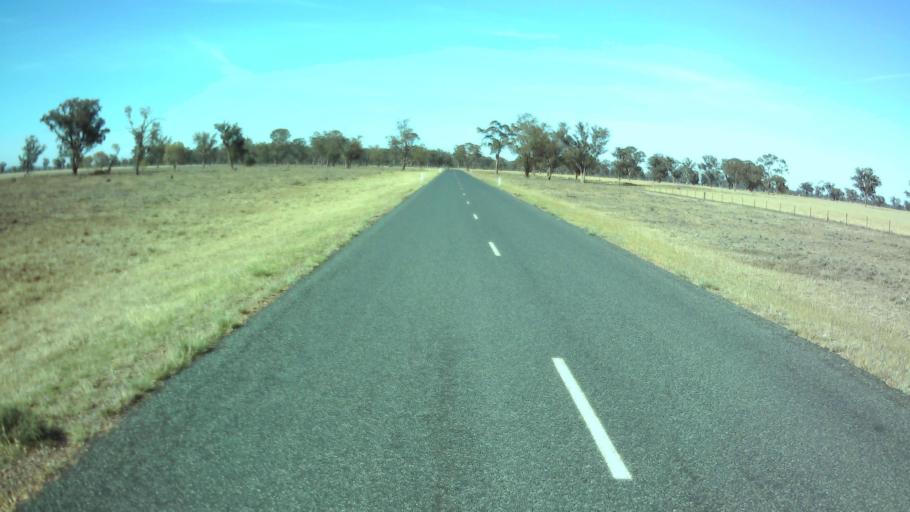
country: AU
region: New South Wales
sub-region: Weddin
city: Grenfell
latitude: -34.0559
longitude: 147.9142
